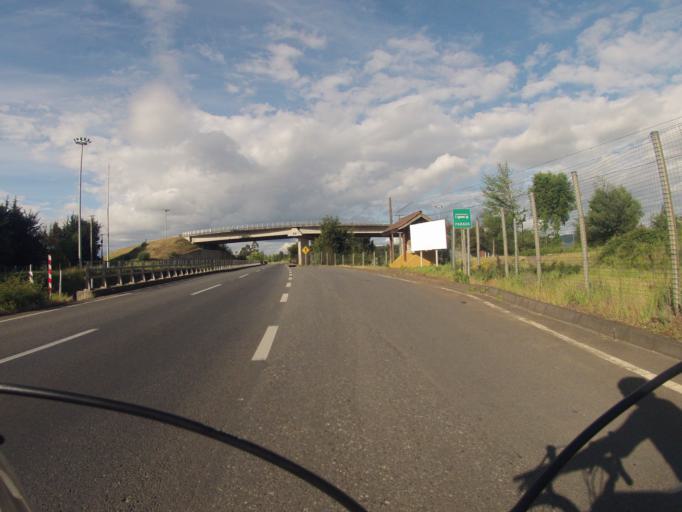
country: CL
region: Araucania
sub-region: Provincia de Cautin
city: Temuco
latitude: -38.7861
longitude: -72.6134
